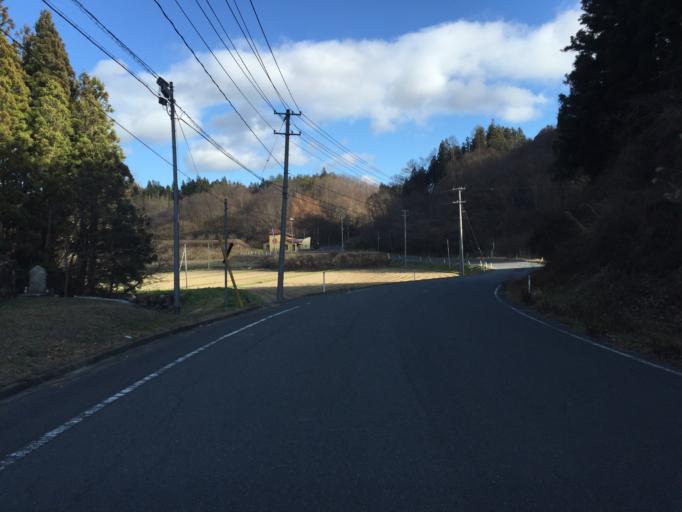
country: JP
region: Fukushima
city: Ishikawa
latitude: 37.2402
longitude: 140.6237
